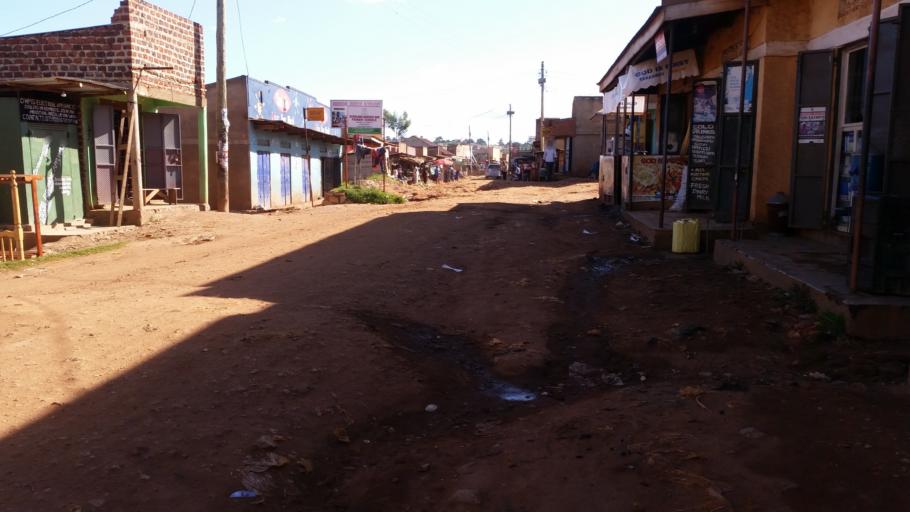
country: UG
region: Central Region
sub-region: Wakiso District
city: Kireka
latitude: 0.3294
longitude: 32.6507
